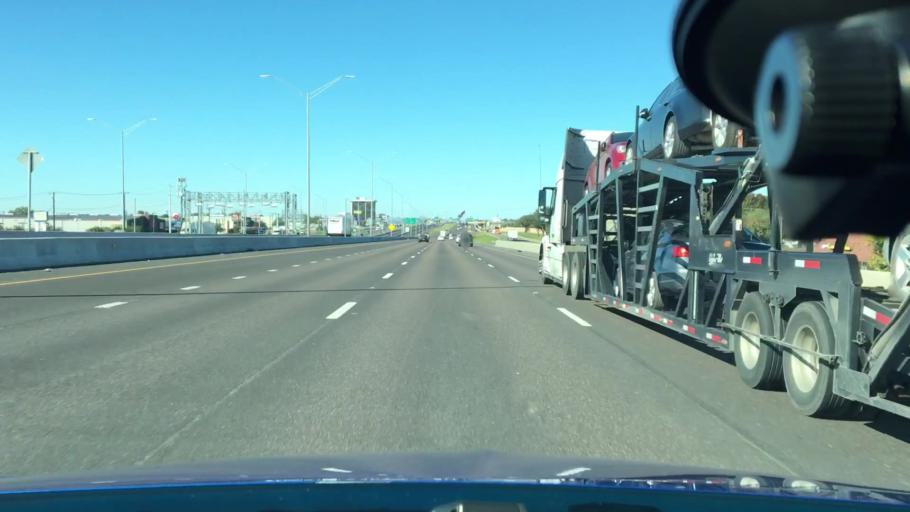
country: US
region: Texas
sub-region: Dallas County
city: Irving
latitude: 32.8375
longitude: -96.9400
